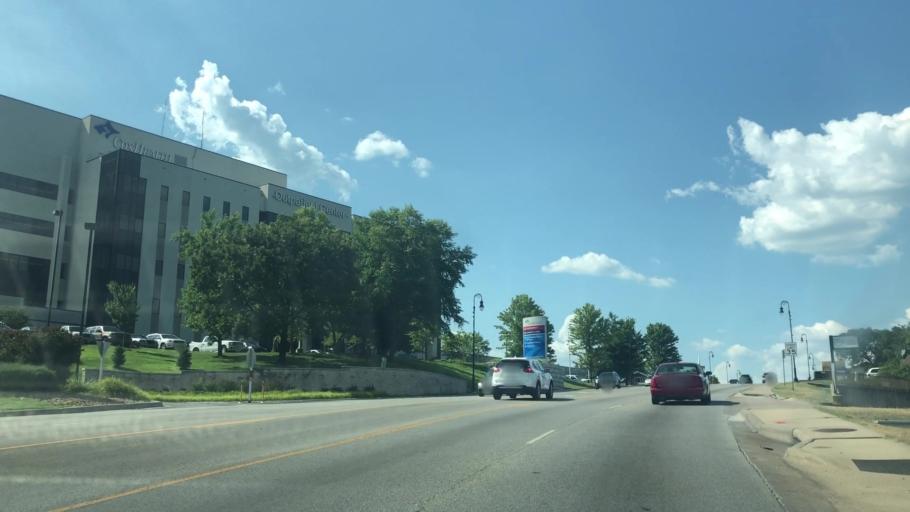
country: US
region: Missouri
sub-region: Taney County
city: Branson
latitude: 36.6508
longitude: -93.2204
